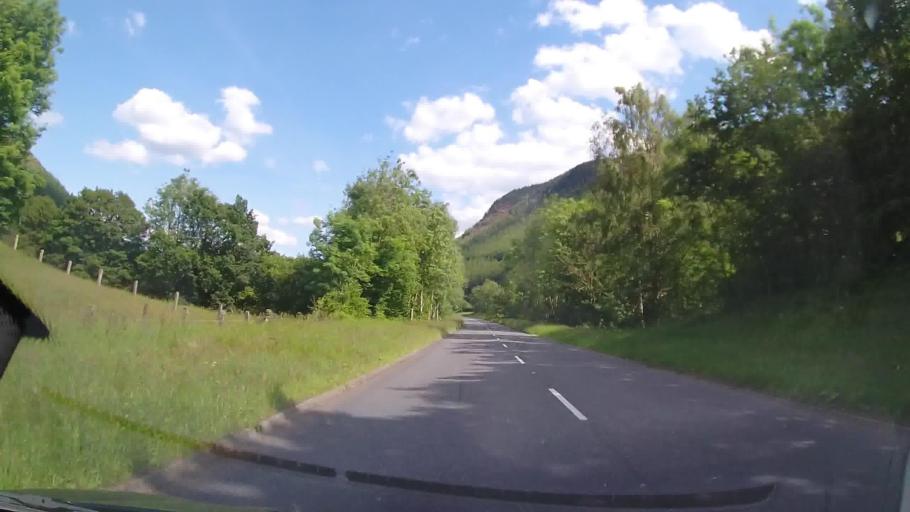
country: GB
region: Wales
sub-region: Gwynedd
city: Corris
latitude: 52.7266
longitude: -3.7106
